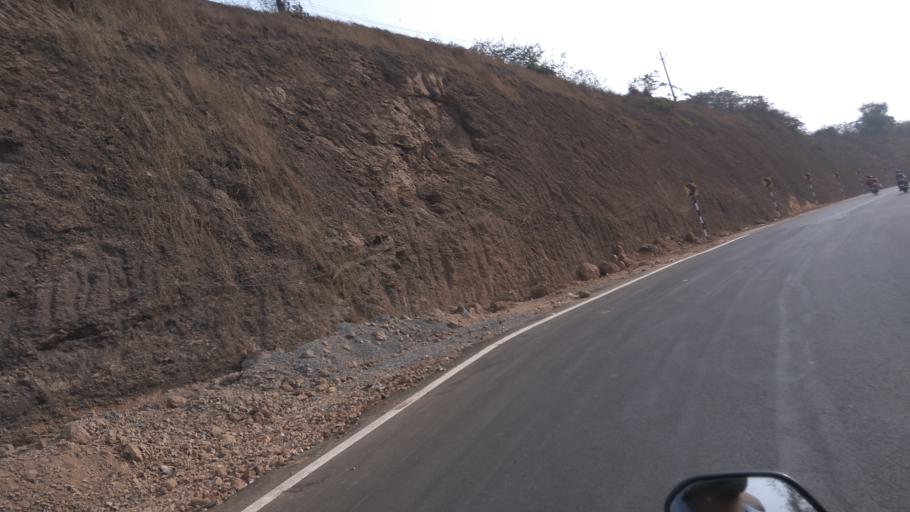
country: IN
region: Goa
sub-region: North Goa
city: Bambolim
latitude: 15.5000
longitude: 73.8647
